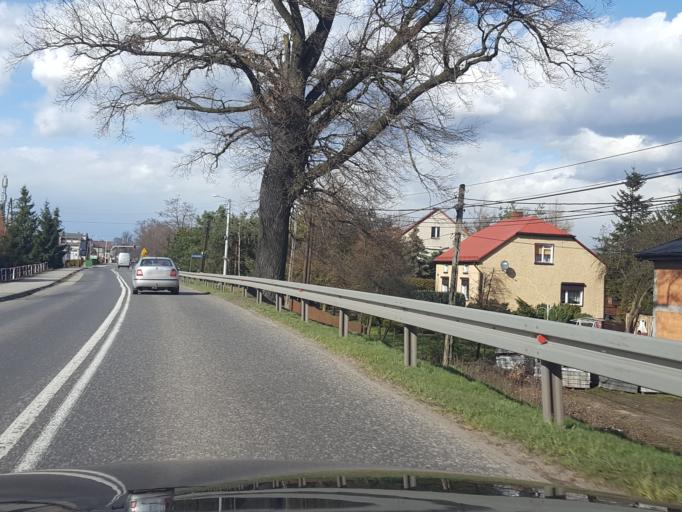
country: PL
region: Silesian Voivodeship
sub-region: Powiat mikolowski
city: Gostyn
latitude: 50.1009
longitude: 18.8832
